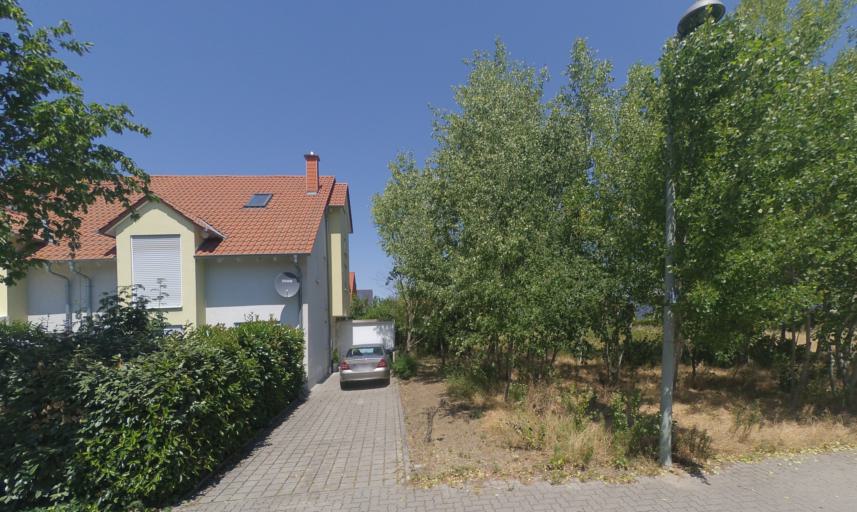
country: DE
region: Rheinland-Pfalz
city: Limburgerhof
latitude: 49.4259
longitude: 8.4004
